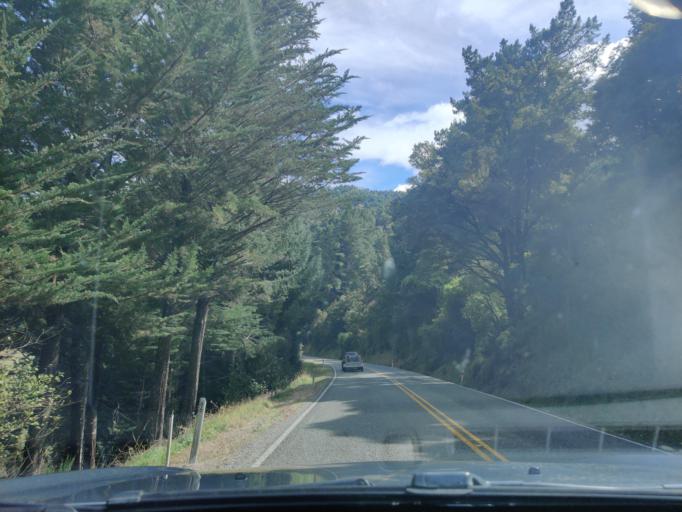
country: NZ
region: Tasman
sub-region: Tasman District
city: Wakefield
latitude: -41.6939
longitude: 172.4956
